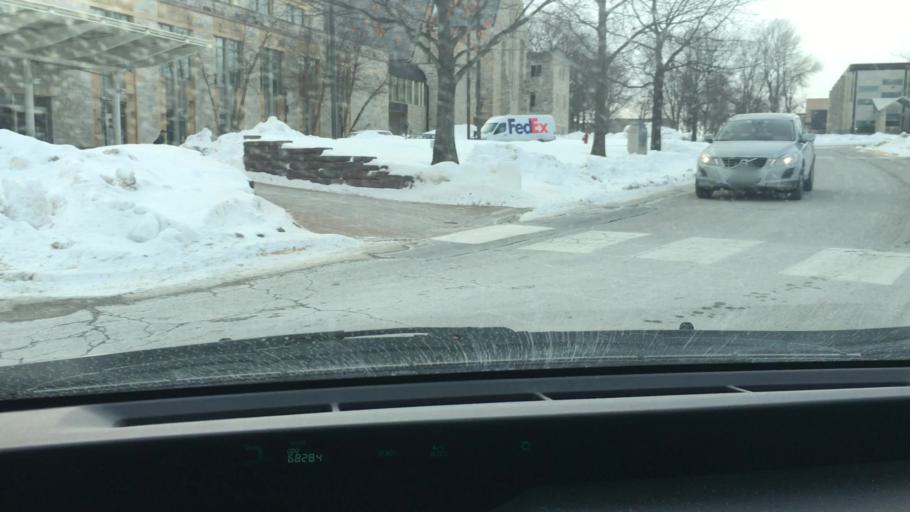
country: US
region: Minnesota
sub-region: Rice County
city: Northfield
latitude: 44.4624
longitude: -93.1827
